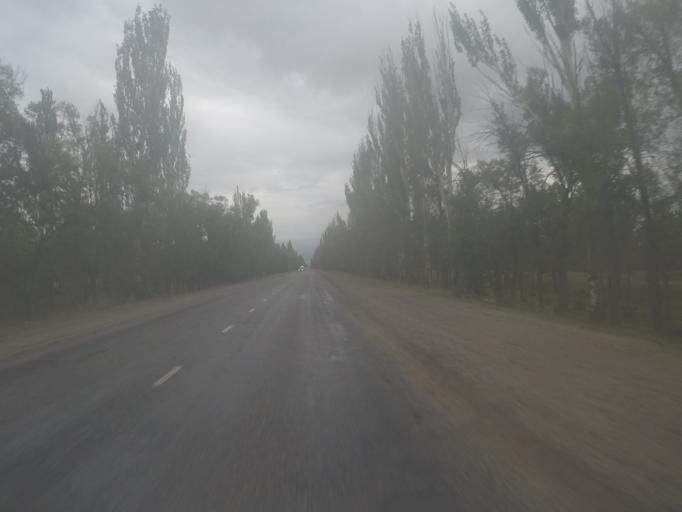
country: KG
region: Ysyk-Koel
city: Tyup
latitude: 42.6357
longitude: 78.3590
